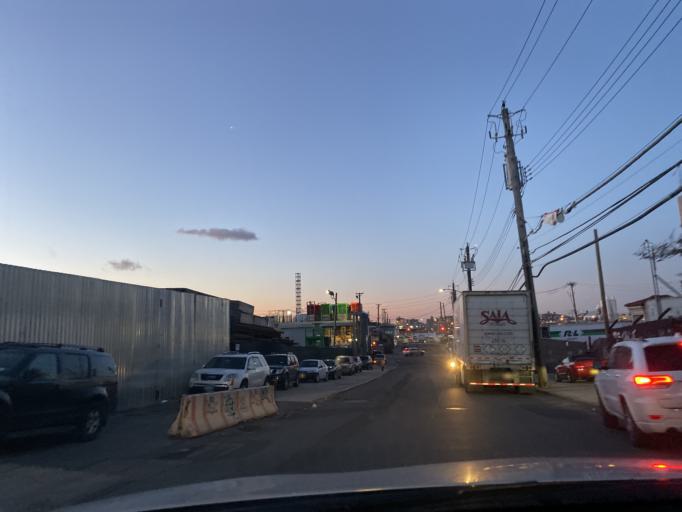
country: US
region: New York
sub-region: Queens County
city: Long Island City
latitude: 40.7297
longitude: -73.9257
